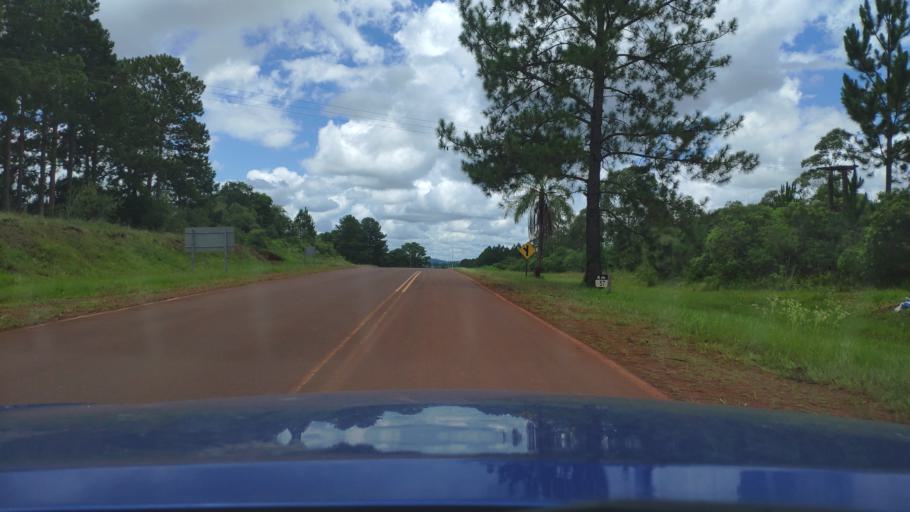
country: AR
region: Misiones
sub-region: Departamento de San Javier
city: San Javier
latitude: -27.8393
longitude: -55.2214
